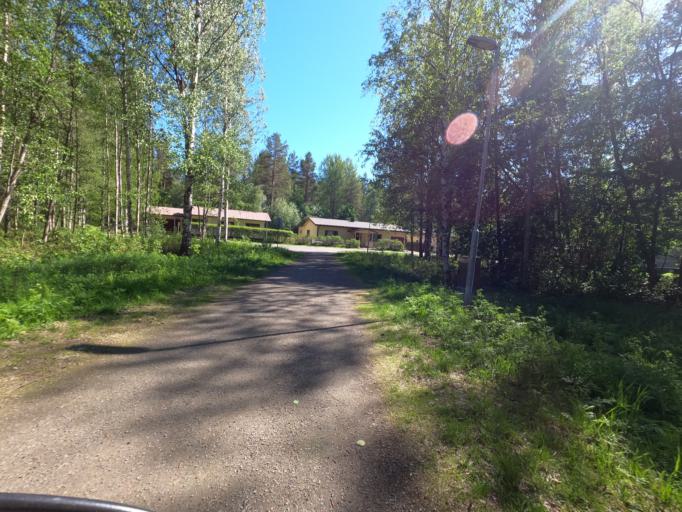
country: FI
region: North Karelia
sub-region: Joensuu
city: Joensuu
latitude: 62.6002
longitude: 29.8209
